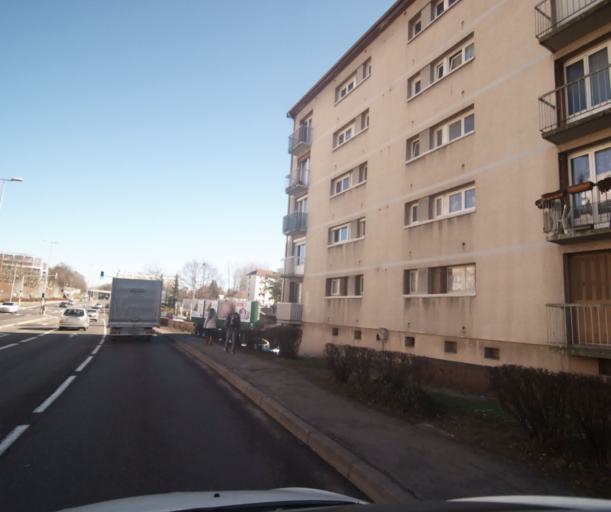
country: FR
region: Franche-Comte
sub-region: Departement du Doubs
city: Besancon
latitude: 47.2507
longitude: 6.0083
